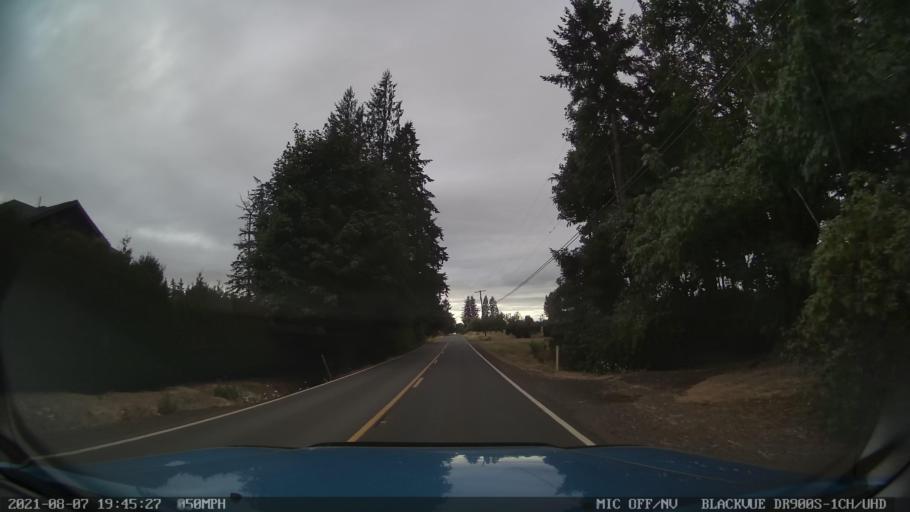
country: US
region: Oregon
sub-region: Marion County
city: Silverton
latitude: 44.9483
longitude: -122.6957
